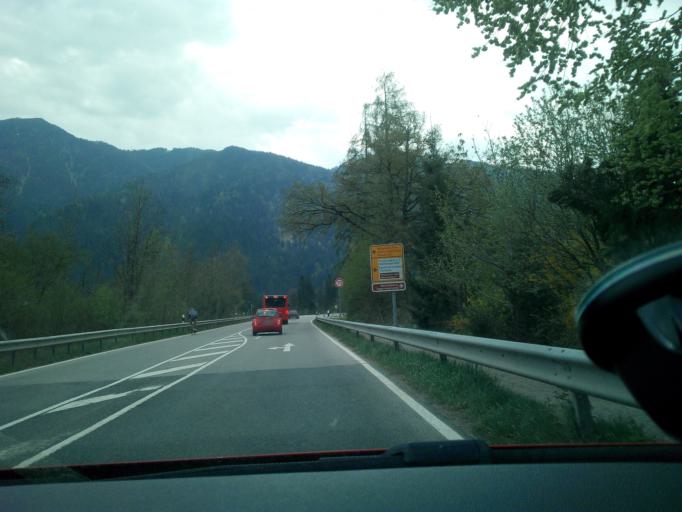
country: DE
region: Bavaria
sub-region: Upper Bavaria
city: Rottach-Egern
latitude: 47.6760
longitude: 11.7602
